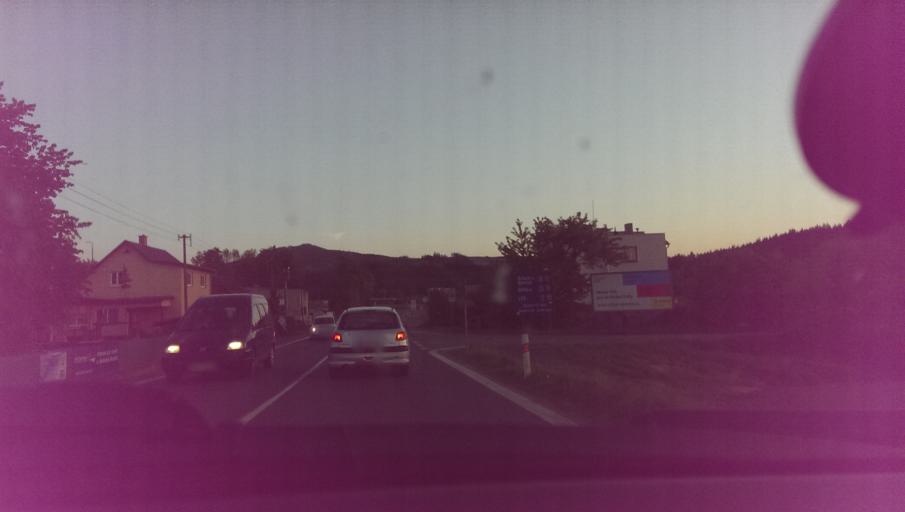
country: CZ
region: Zlin
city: Jablunka
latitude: 49.3789
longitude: 17.9468
